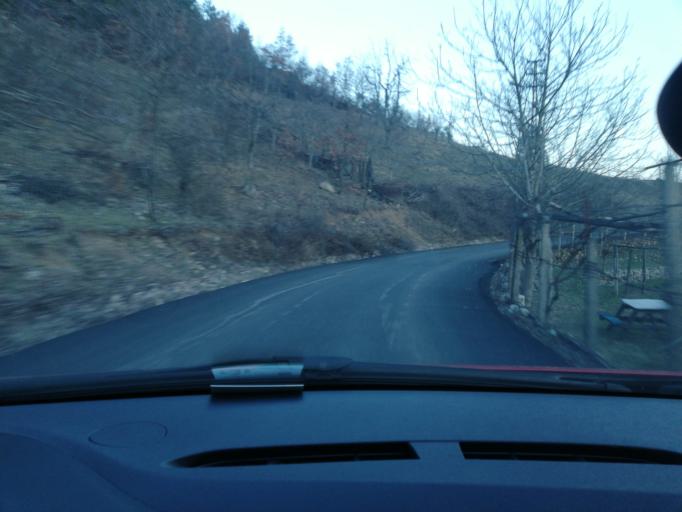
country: TR
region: Karabuk
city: Safranbolu
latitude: 41.2721
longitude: 32.6319
